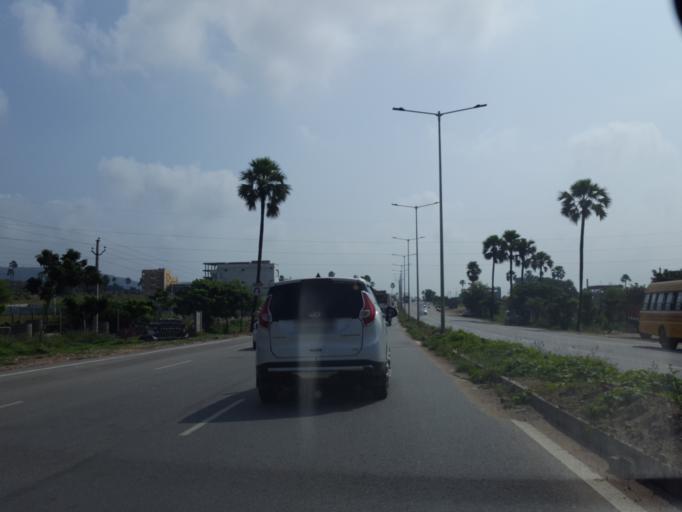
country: IN
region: Telangana
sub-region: Rangareddi
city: Lal Bahadur Nagar
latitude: 17.3093
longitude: 78.6892
